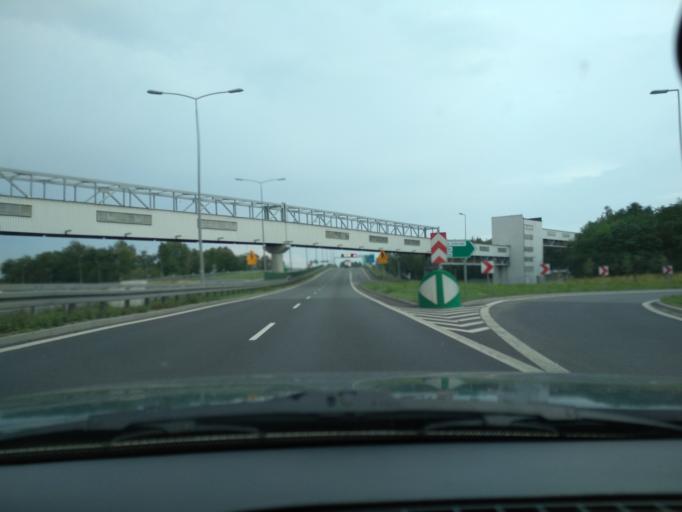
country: PL
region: Silesian Voivodeship
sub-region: Gliwice
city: Gliwice
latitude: 50.2843
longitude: 18.7103
